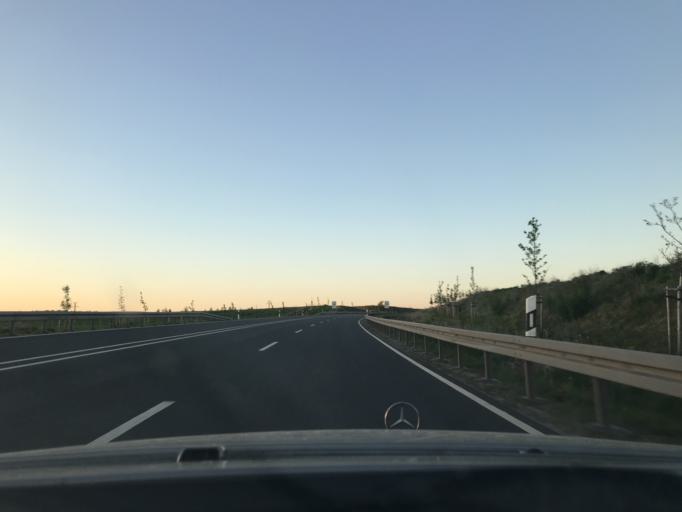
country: DE
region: Thuringia
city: Heilbad Heiligenstadt
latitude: 51.3833
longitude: 10.1150
